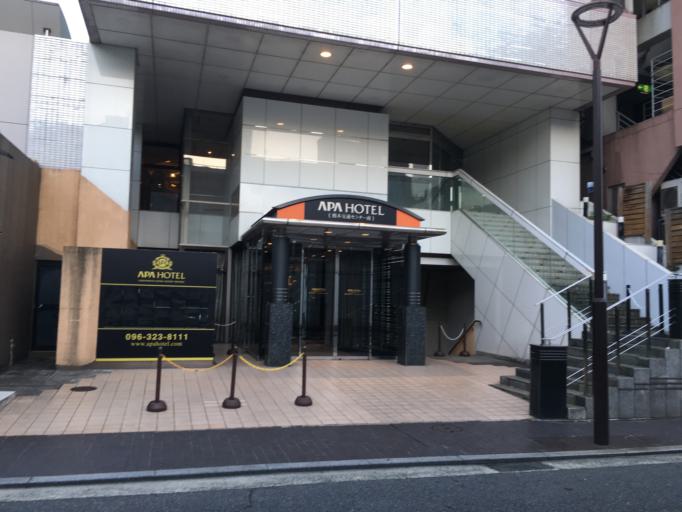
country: JP
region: Kumamoto
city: Kumamoto
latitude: 32.7971
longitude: 130.7038
